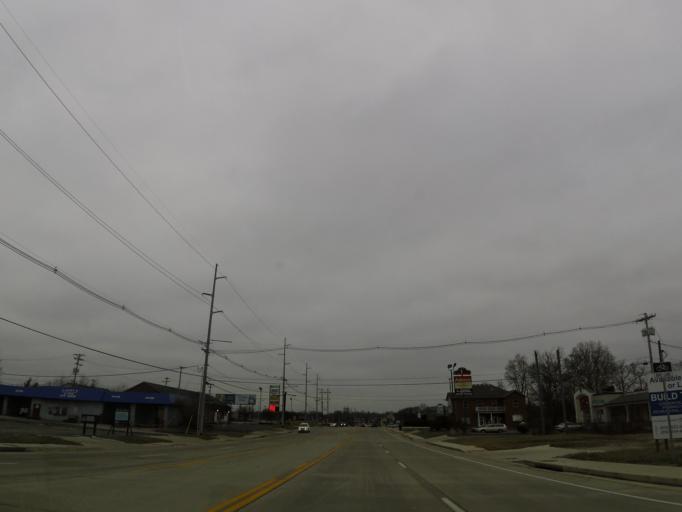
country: US
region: Kentucky
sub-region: Franklin County
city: Frankfort
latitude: 38.1824
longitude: -84.8912
